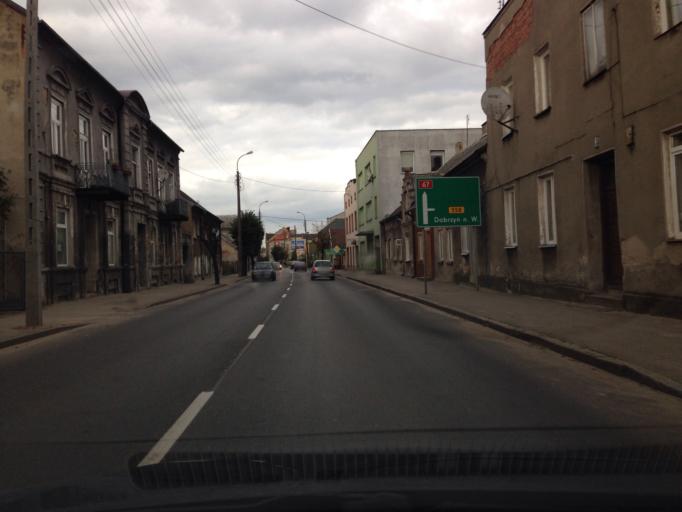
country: PL
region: Kujawsko-Pomorskie
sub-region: Powiat lipnowski
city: Lipno
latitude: 52.8411
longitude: 19.1762
